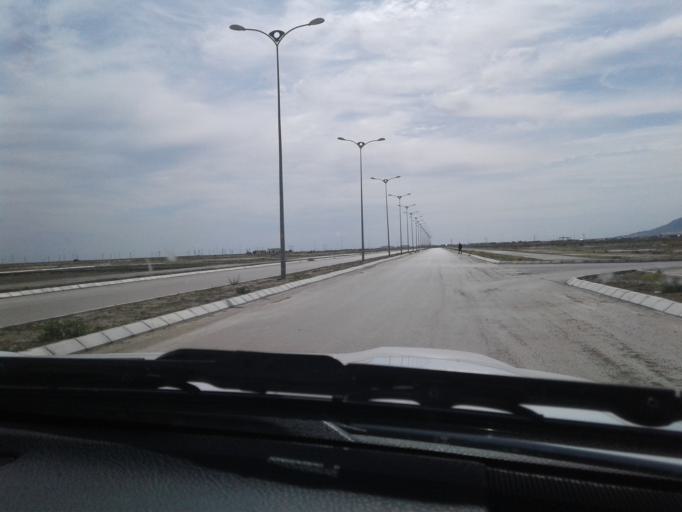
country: TM
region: Balkan
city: Gazanjyk
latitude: 39.2671
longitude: 55.4912
